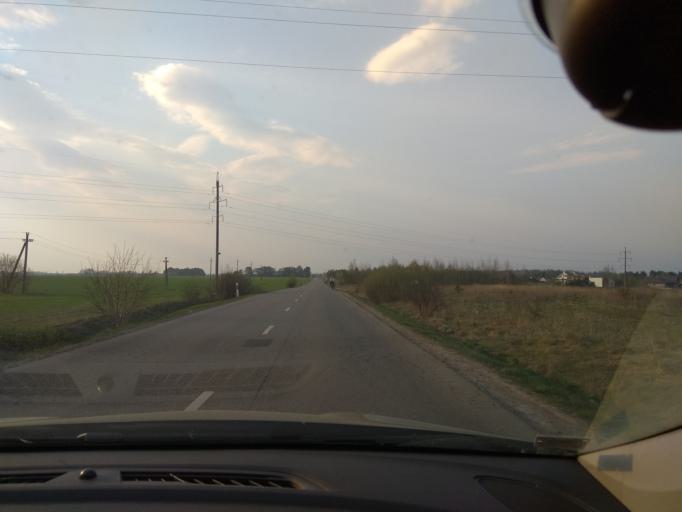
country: LT
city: Lentvaris
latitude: 54.6140
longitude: 25.1193
